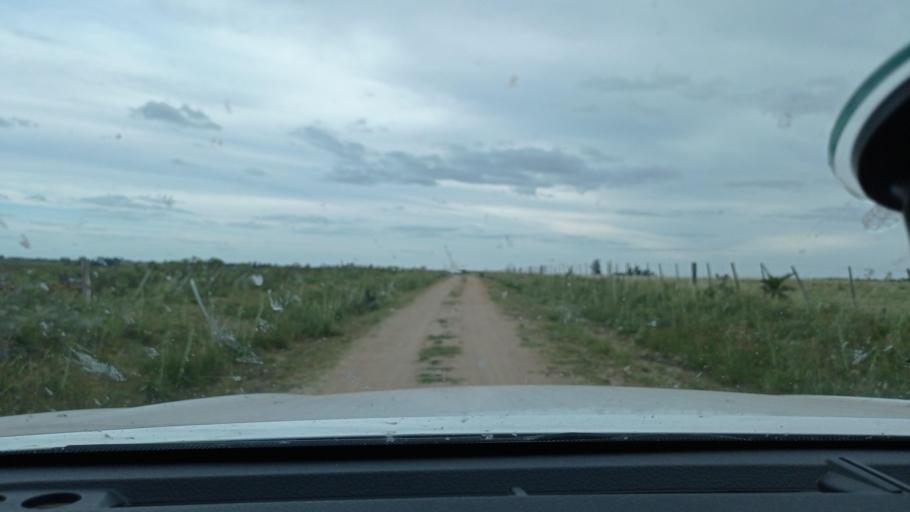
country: UY
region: Florida
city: Casupa
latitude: -34.1284
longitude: -55.8012
